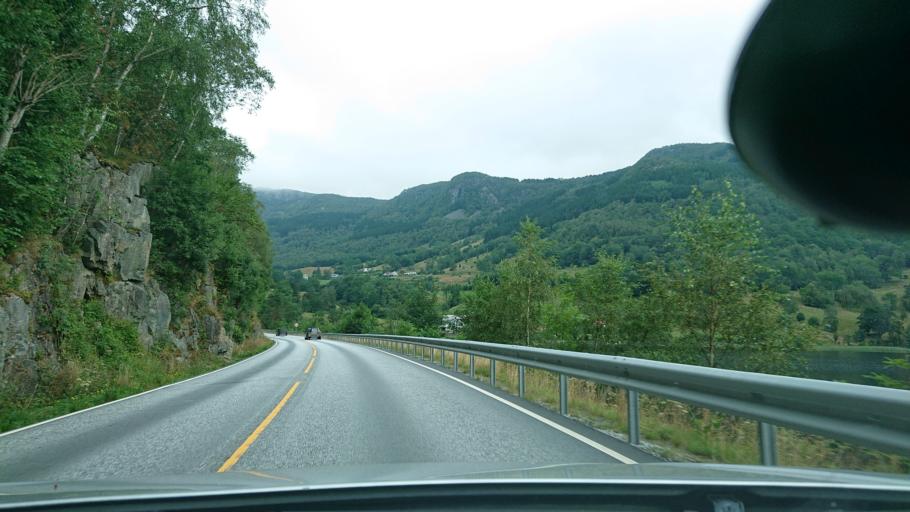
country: NO
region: Rogaland
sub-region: Hjelmeland
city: Hjelmelandsvagen
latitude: 59.1616
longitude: 6.1741
